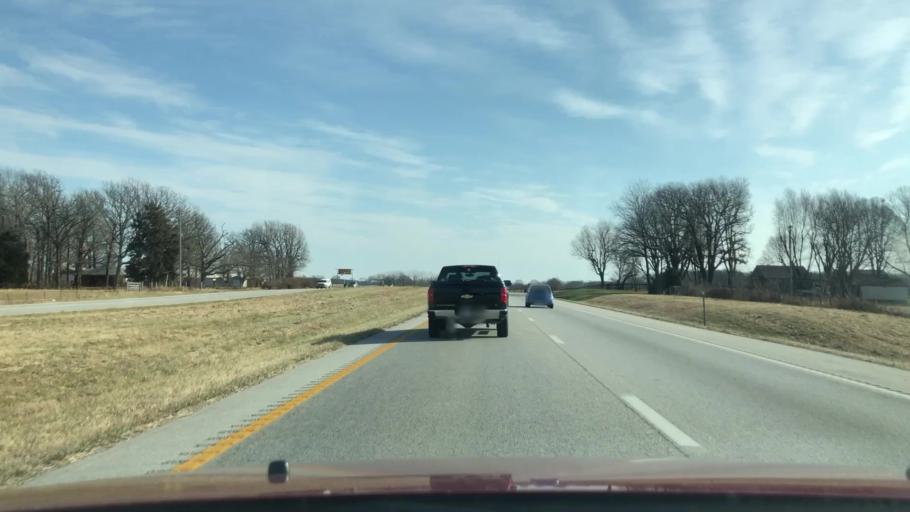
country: US
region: Missouri
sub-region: Webster County
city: Rogersville
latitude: 37.1185
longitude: -93.1114
